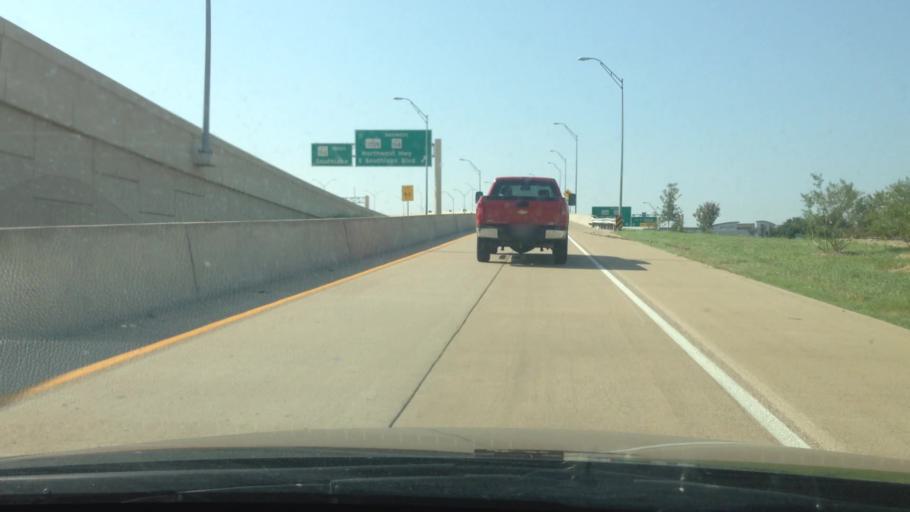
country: US
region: Texas
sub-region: Tarrant County
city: Grapevine
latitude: 32.9274
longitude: -97.0906
